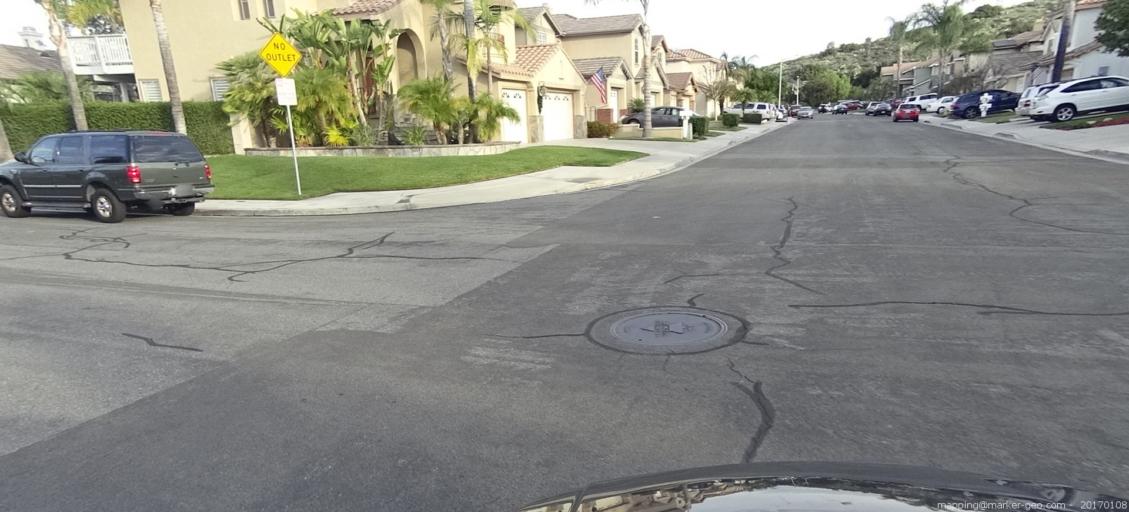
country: US
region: California
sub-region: Orange County
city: Las Flores
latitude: 33.5963
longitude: -117.6223
